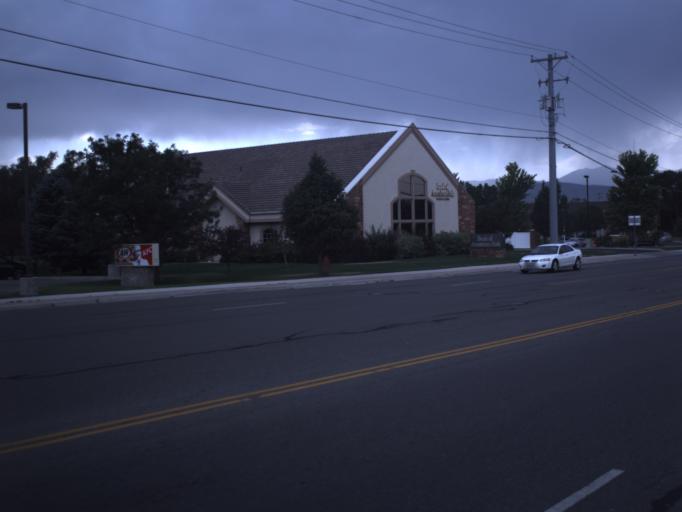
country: US
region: Utah
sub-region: Salt Lake County
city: Draper
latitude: 40.5270
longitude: -111.8723
